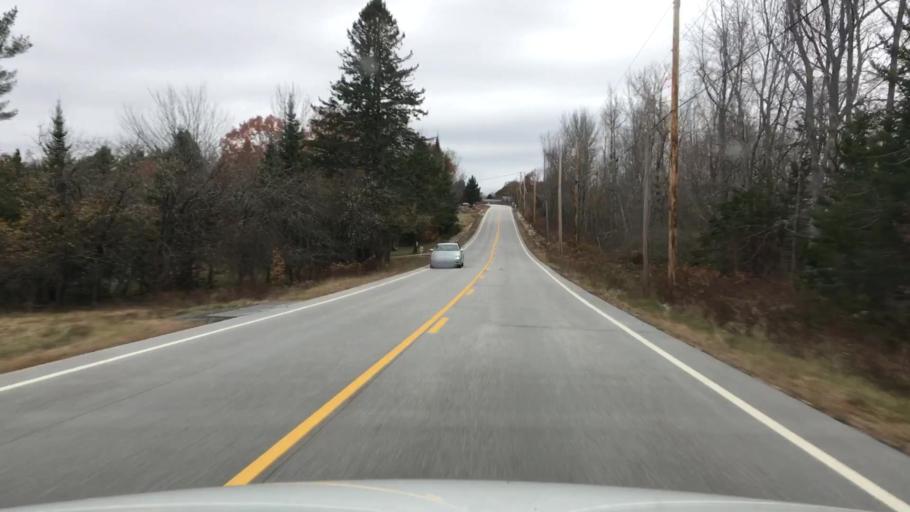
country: US
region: Maine
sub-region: Hancock County
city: Penobscot
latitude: 44.5160
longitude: -68.6582
